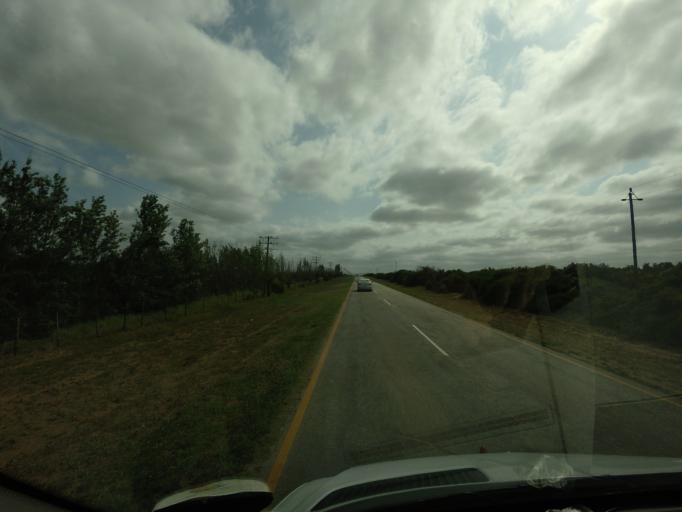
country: ZA
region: Eastern Cape
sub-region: Cacadu District Municipality
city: Kirkwood
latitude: -33.4890
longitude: 25.7053
